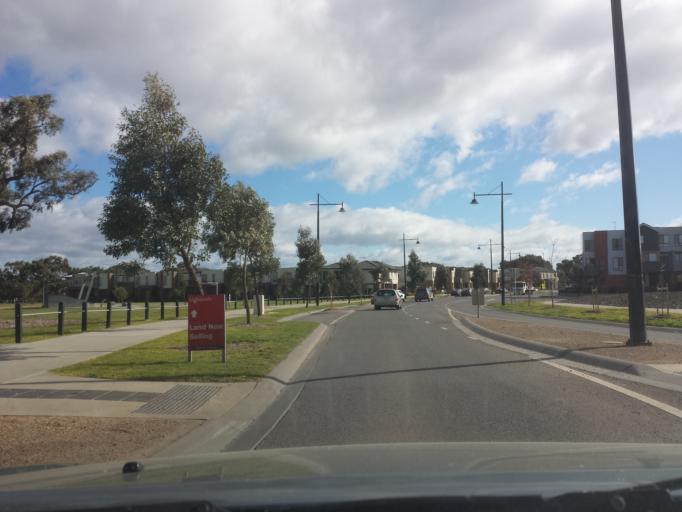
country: AU
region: Victoria
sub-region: Hume
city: Craigieburn
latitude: -37.5754
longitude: 144.9185
